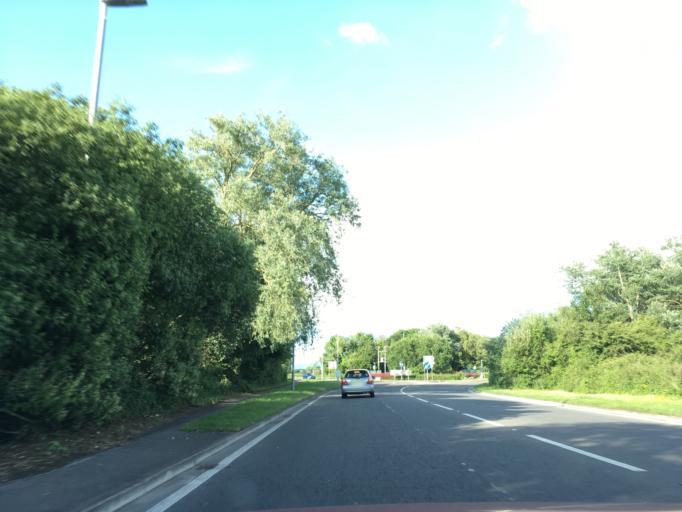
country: GB
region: England
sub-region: Somerset
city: Highbridge
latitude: 51.2280
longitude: -2.9637
